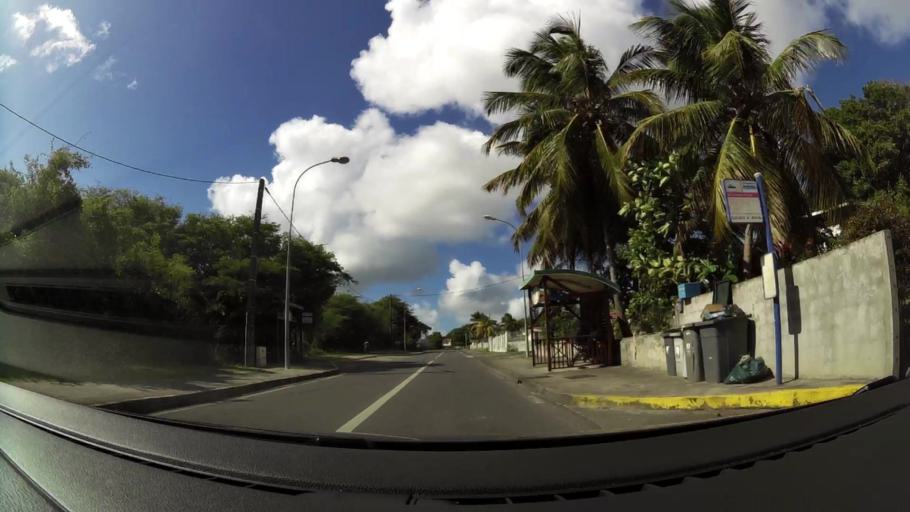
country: GP
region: Guadeloupe
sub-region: Guadeloupe
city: Saint-Francois
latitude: 16.2523
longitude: -61.2880
